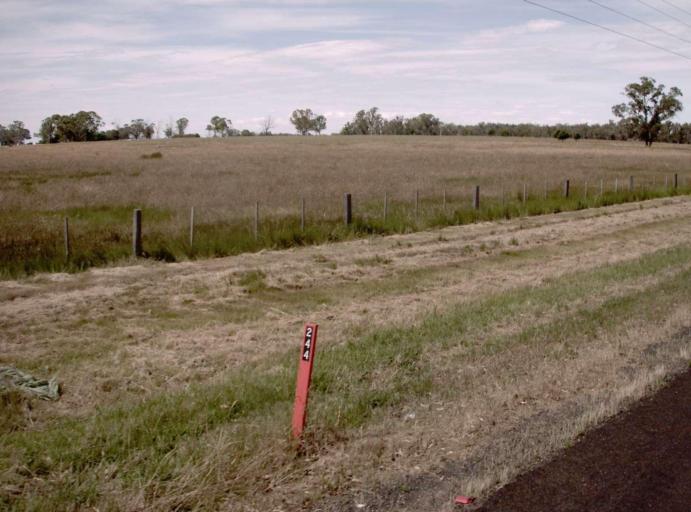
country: AU
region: Victoria
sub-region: Wellington
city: Sale
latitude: -37.9241
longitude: 147.2341
